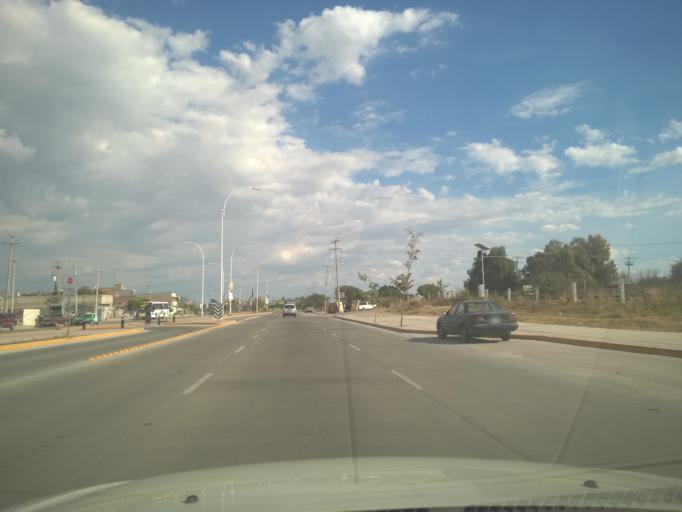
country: MX
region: Guanajuato
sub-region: Leon
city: San Jose de Duran (Los Troncoso)
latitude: 21.0657
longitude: -101.6339
